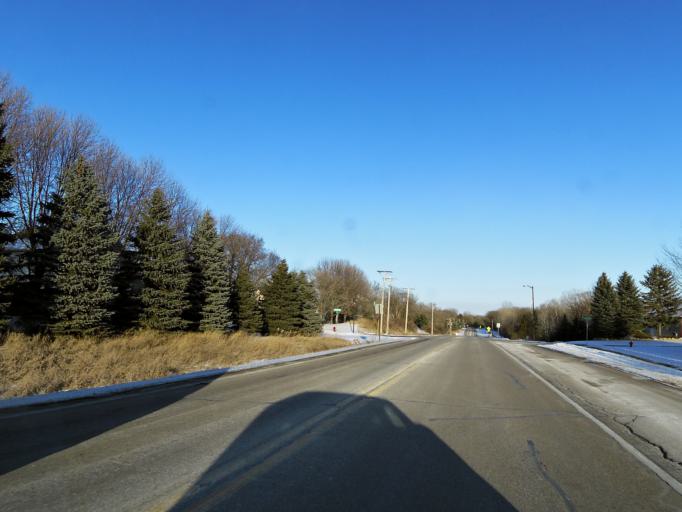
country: US
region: Minnesota
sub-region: Dakota County
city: Lakeville
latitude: 44.6536
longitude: -93.2805
